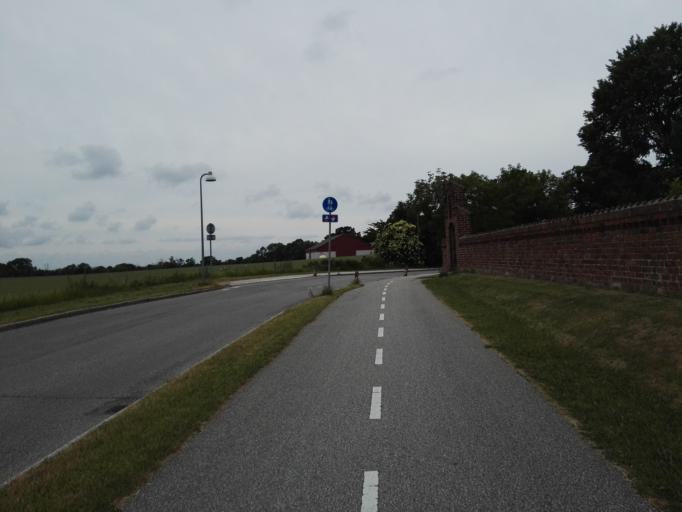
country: DK
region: Capital Region
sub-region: Egedal Kommune
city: Smorumnedre
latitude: 55.7335
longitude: 12.2782
